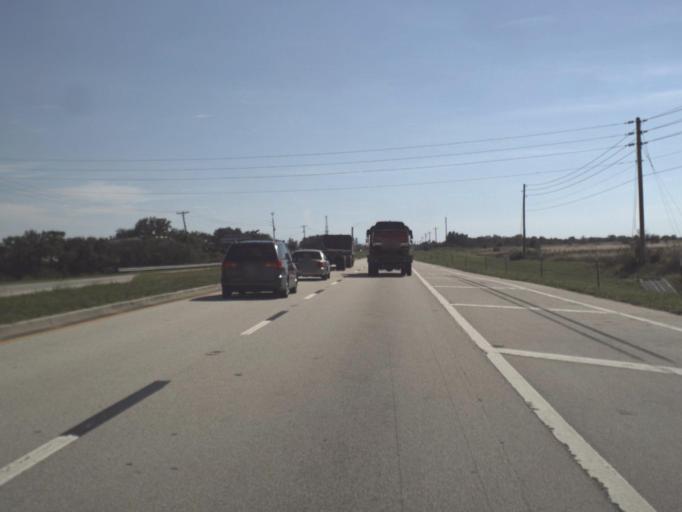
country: US
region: Florida
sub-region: Highlands County
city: Sebring
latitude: 27.4256
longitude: -81.4178
